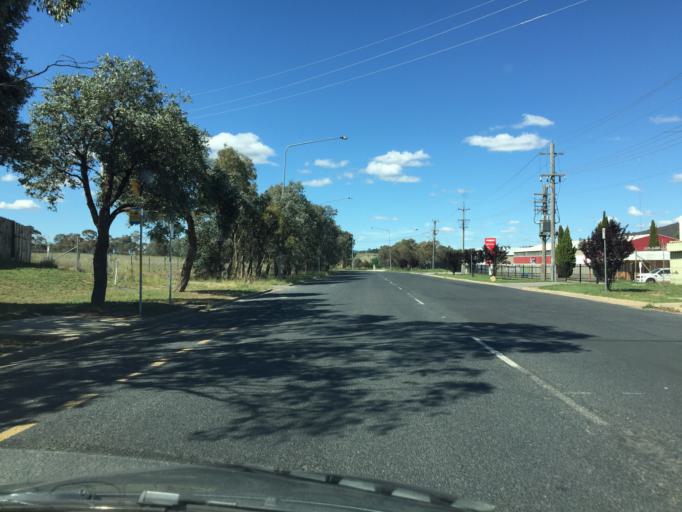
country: AU
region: Australian Capital Territory
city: Macarthur
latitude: -35.3862
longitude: 149.1733
